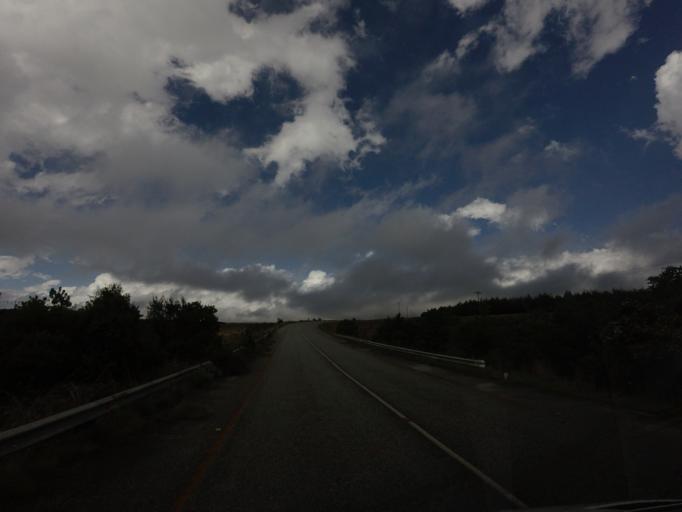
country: ZA
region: Mpumalanga
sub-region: Ehlanzeni District
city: Graksop
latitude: -24.8574
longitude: 30.8700
